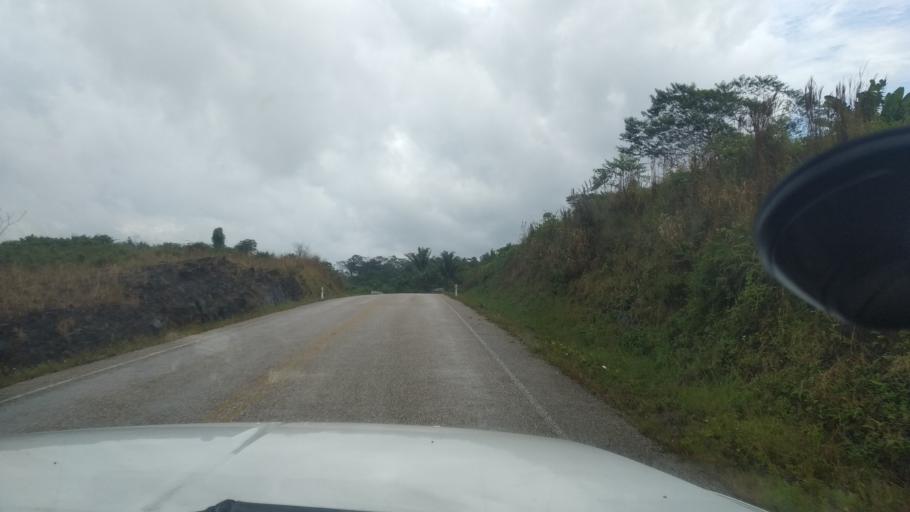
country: GT
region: Peten
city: San Luis
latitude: 16.1962
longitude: -89.1612
